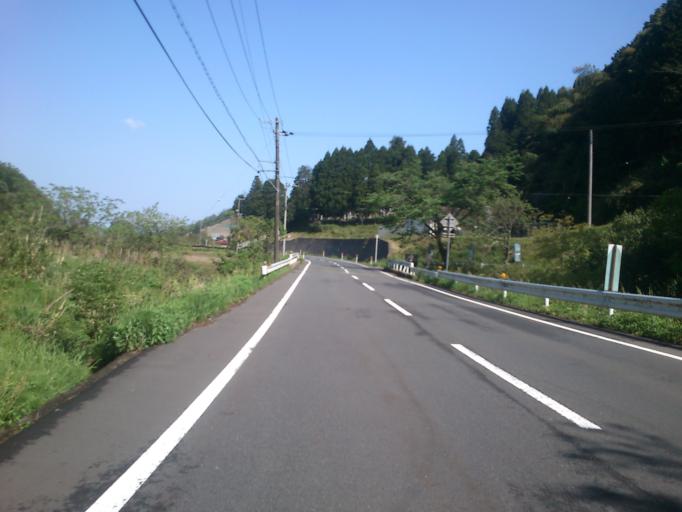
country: JP
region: Kyoto
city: Miyazu
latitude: 35.6454
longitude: 135.1292
